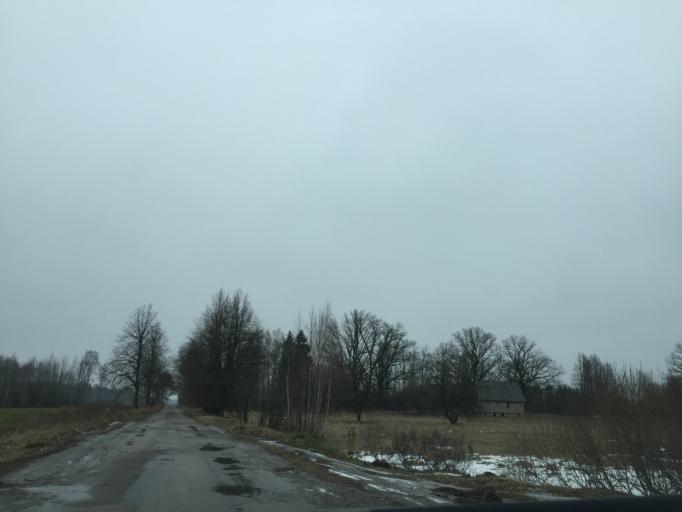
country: LV
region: Lecava
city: Iecava
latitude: 56.6021
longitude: 24.0717
